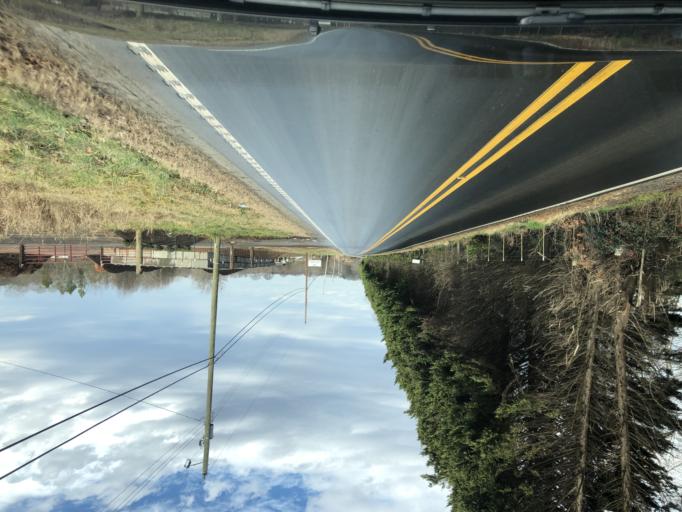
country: US
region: South Carolina
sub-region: Greenville County
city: Five Forks
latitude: 34.8641
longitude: -82.1991
